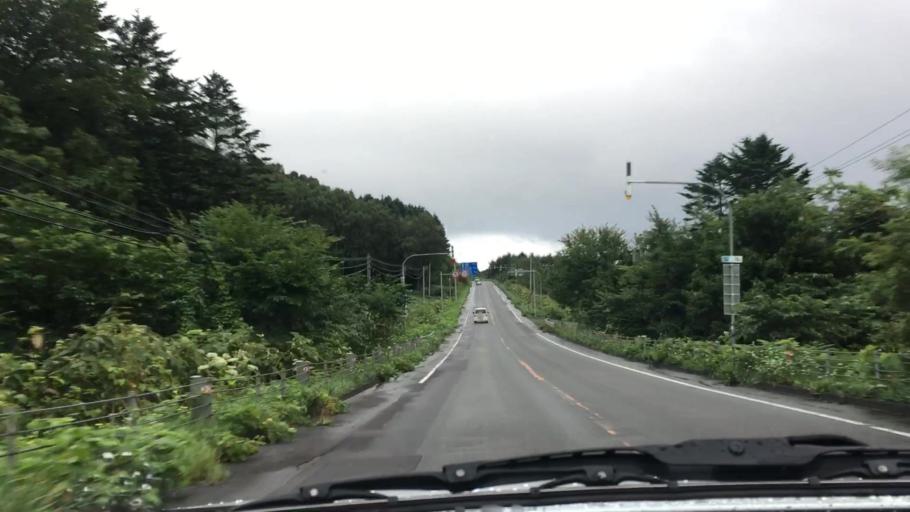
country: JP
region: Hokkaido
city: Niseko Town
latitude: 42.6042
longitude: 140.7260
